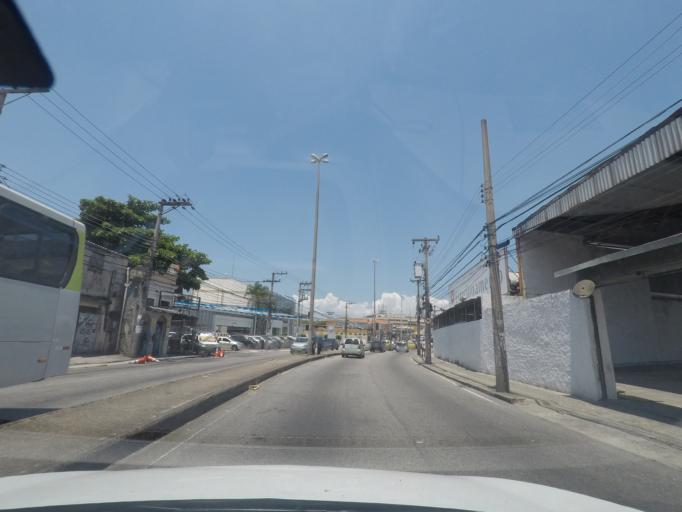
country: BR
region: Rio de Janeiro
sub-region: Rio De Janeiro
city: Rio de Janeiro
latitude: -22.8856
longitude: -43.3012
